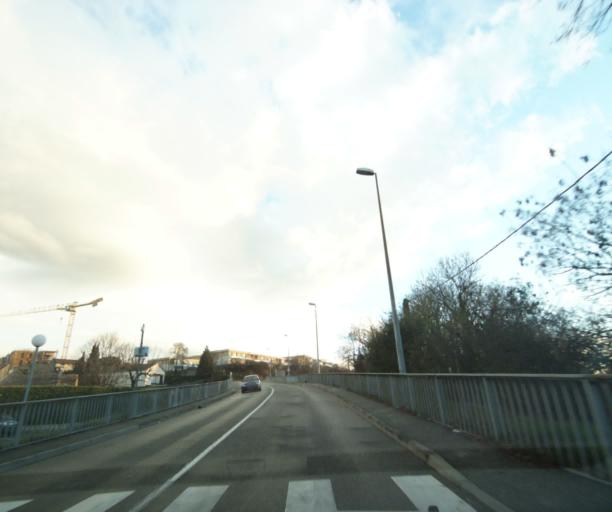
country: FR
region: Rhone-Alpes
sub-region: Departement de la Drome
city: Bourg-les-Valence
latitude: 44.9495
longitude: 4.9037
